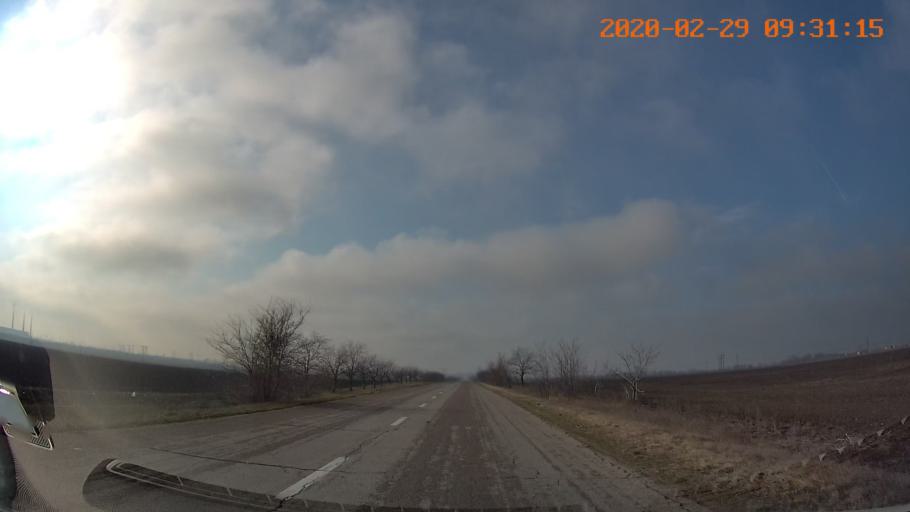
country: MD
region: Telenesti
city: Dnestrovsc
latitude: 46.6555
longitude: 29.9123
